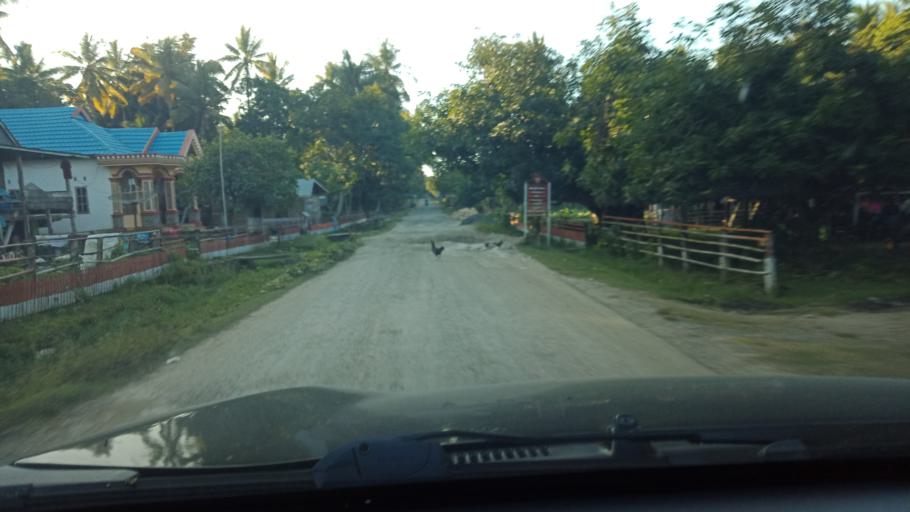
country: ID
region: South Sulawesi
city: Watampone
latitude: -4.4253
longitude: 120.3328
